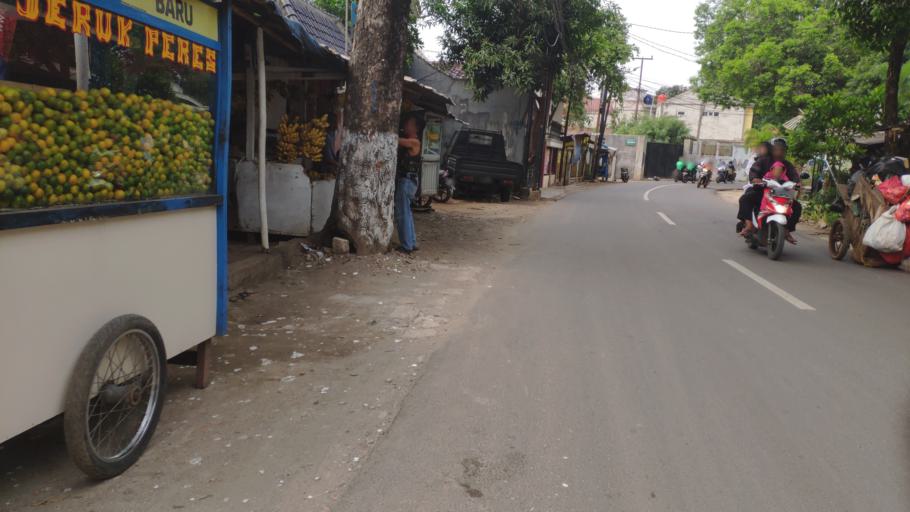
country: ID
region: West Java
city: Depok
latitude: -6.3450
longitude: 106.8119
